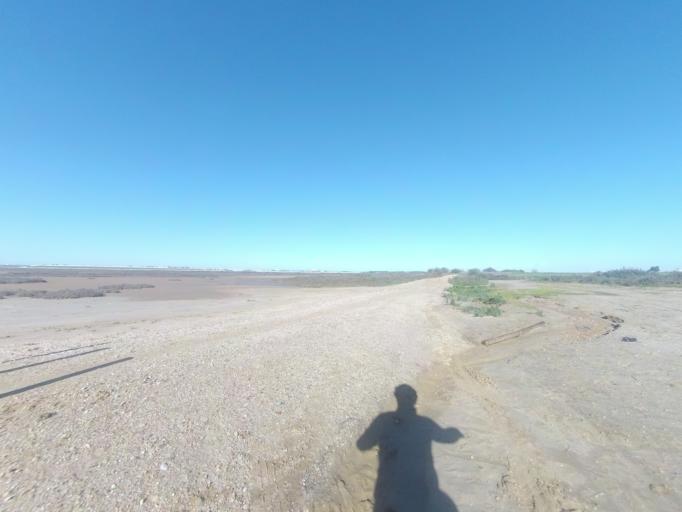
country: ES
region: Andalusia
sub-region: Provincia de Huelva
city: Palos de la Frontera
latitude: 37.2391
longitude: -6.8916
